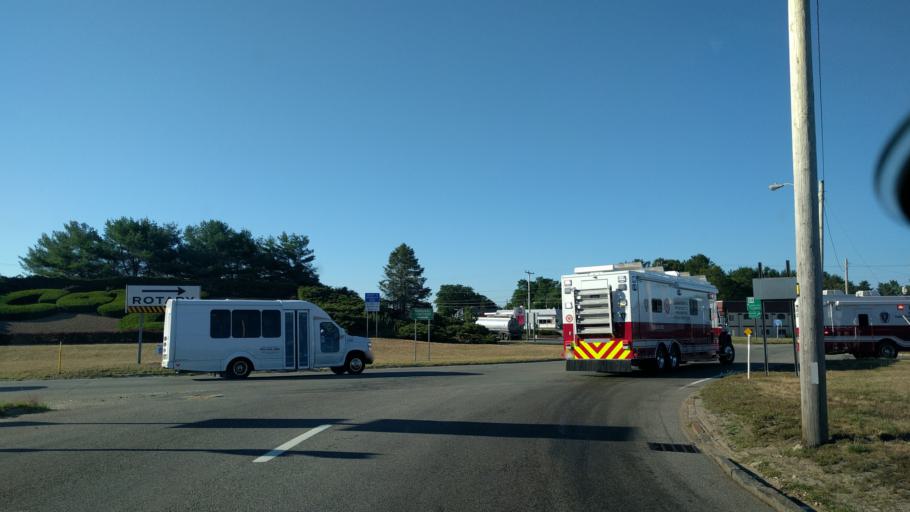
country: US
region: Massachusetts
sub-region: Barnstable County
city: Bourne
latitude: 41.7438
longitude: -70.5870
